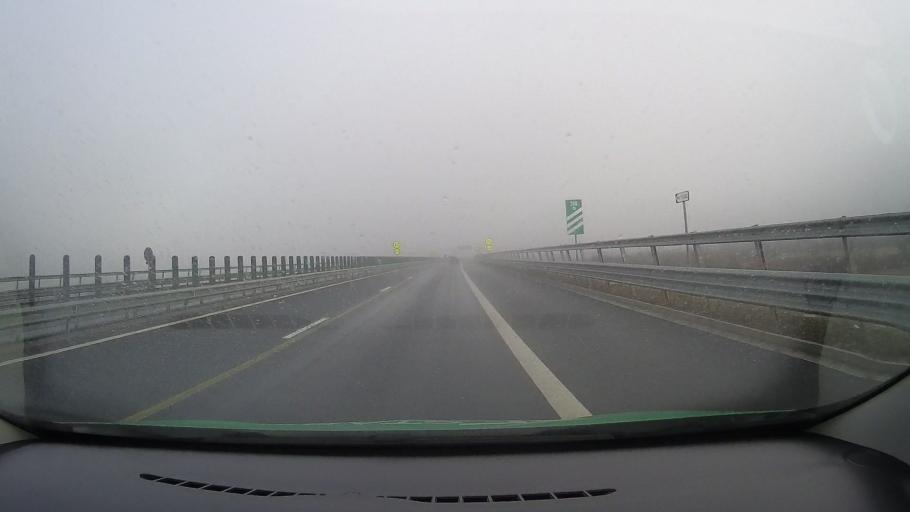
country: RO
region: Timis
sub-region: Comuna Margina
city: Margina
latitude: 45.8544
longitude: 22.2404
